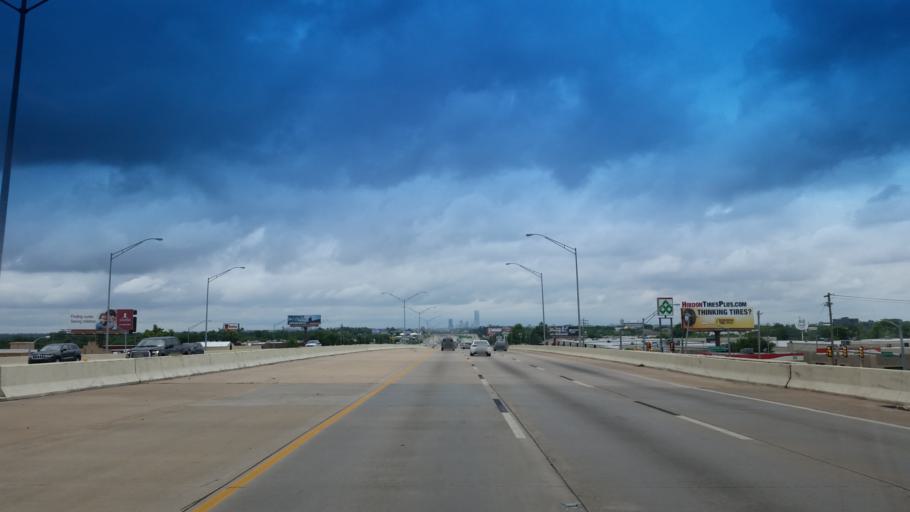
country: US
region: Oklahoma
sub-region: Oklahoma County
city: Nichols Hills
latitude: 35.5521
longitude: -97.5140
